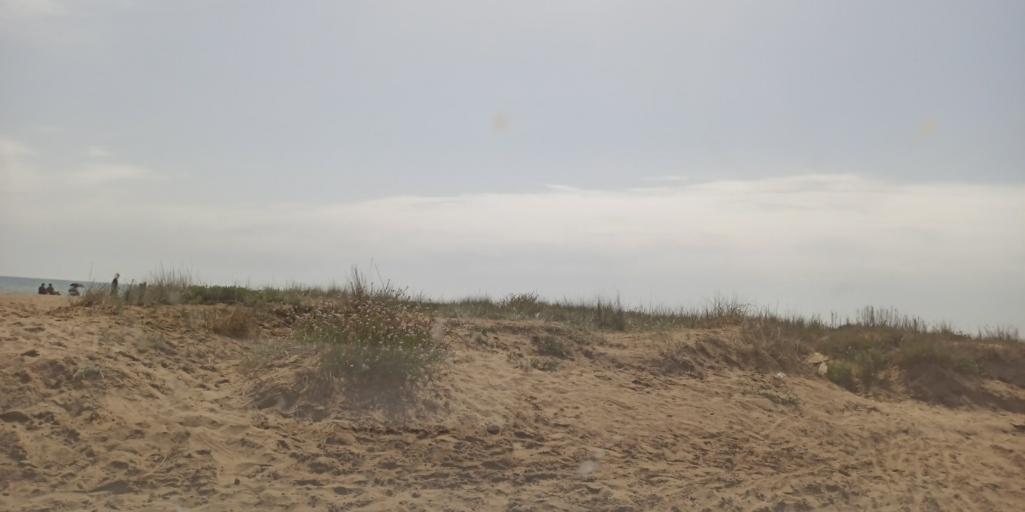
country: ES
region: Catalonia
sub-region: Provincia de Tarragona
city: Deltebre
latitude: 40.6284
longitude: 0.7415
